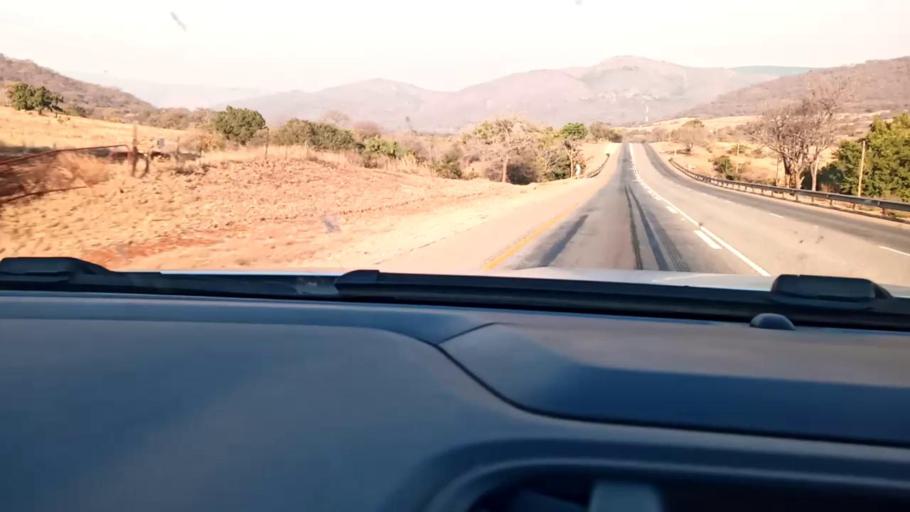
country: ZA
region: Limpopo
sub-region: Mopani District Municipality
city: Duiwelskloof
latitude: -23.6397
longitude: 30.1554
